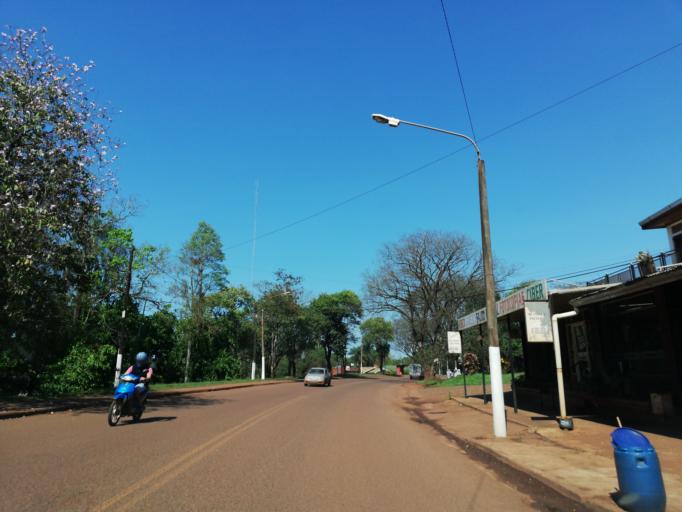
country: AR
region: Misiones
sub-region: Departamento de Eldorado
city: Eldorado
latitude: -26.4079
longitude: -54.6416
